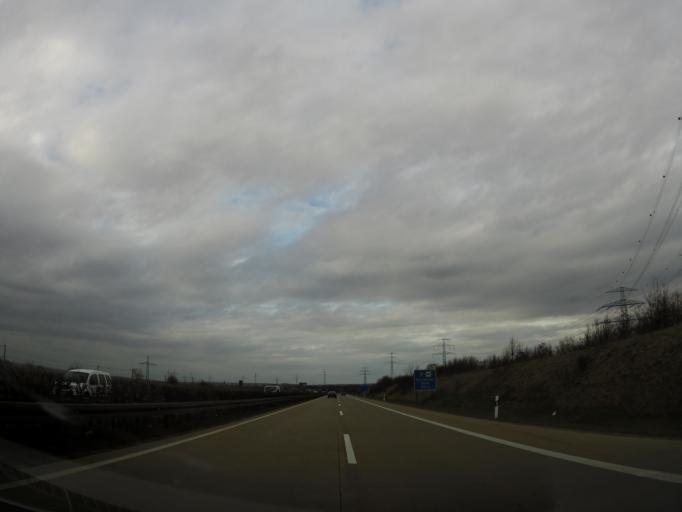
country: DE
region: Thuringia
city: Dornheim
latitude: 50.8284
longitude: 11.0070
